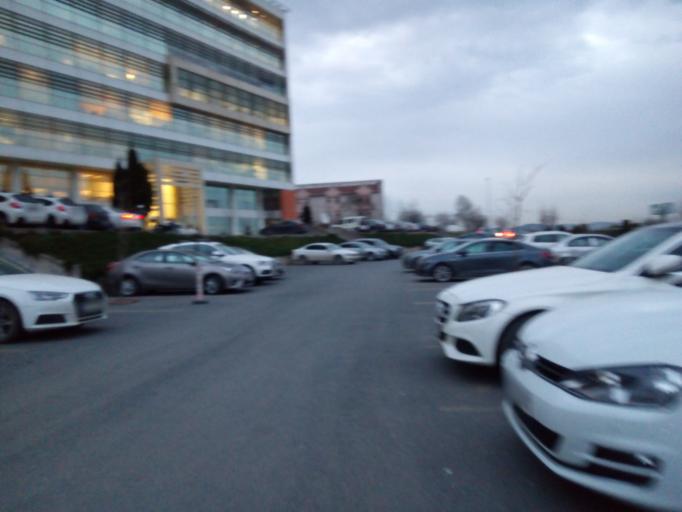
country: TR
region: Istanbul
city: Sisli
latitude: 41.1080
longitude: 29.0336
